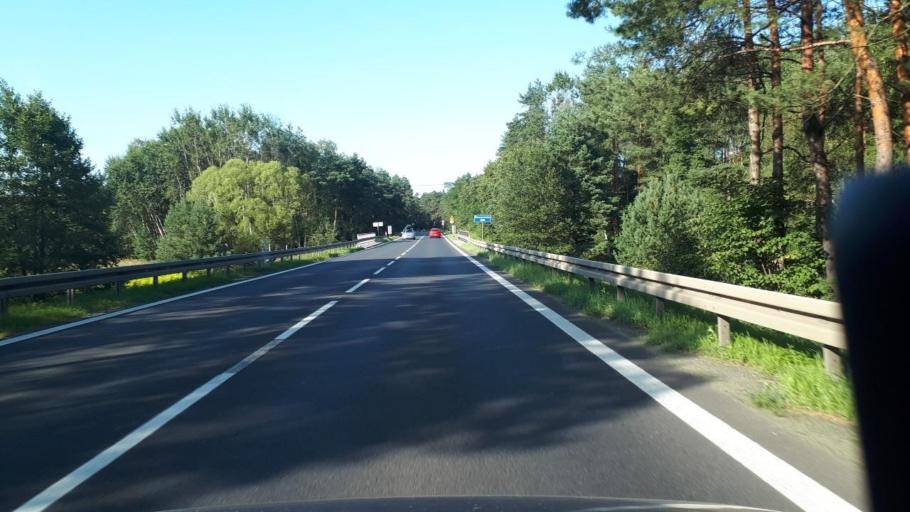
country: PL
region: Silesian Voivodeship
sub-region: Powiat tarnogorski
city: Tworog
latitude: 50.5393
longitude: 18.7167
